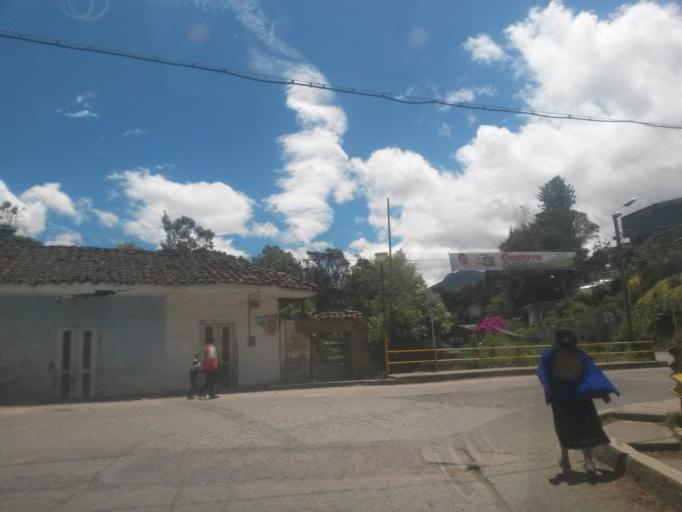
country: CO
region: Cauca
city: Silvia
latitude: 2.6105
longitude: -76.3810
